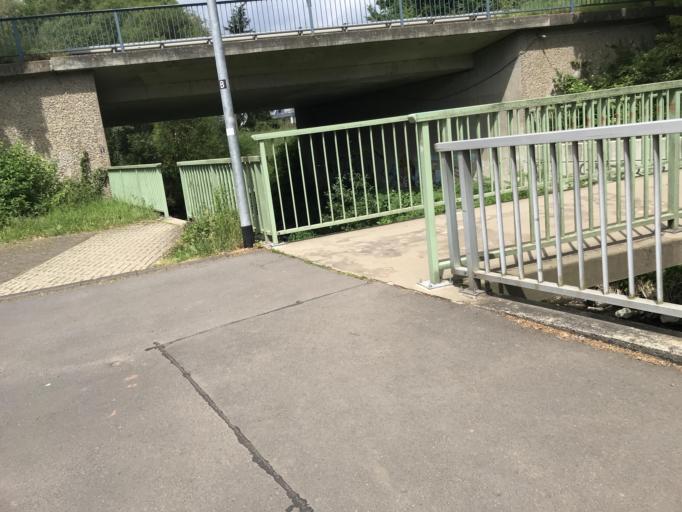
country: DE
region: Hesse
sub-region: Regierungsbezirk Kassel
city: Baunatal
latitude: 51.2585
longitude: 9.4019
